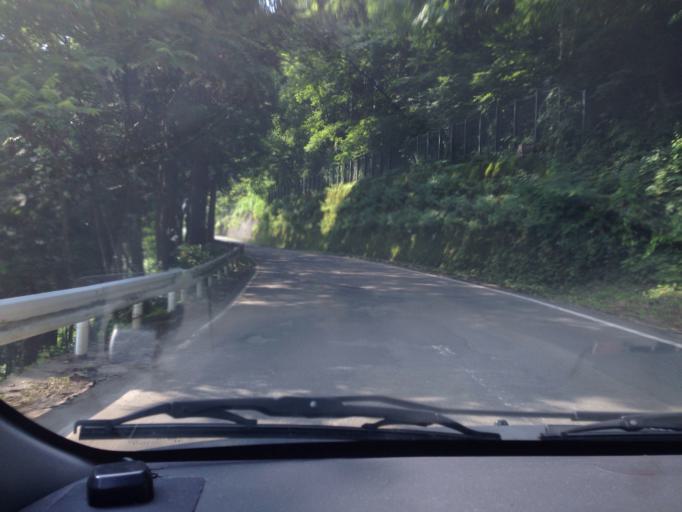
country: JP
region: Fukushima
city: Kitakata
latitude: 37.4346
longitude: 139.5326
